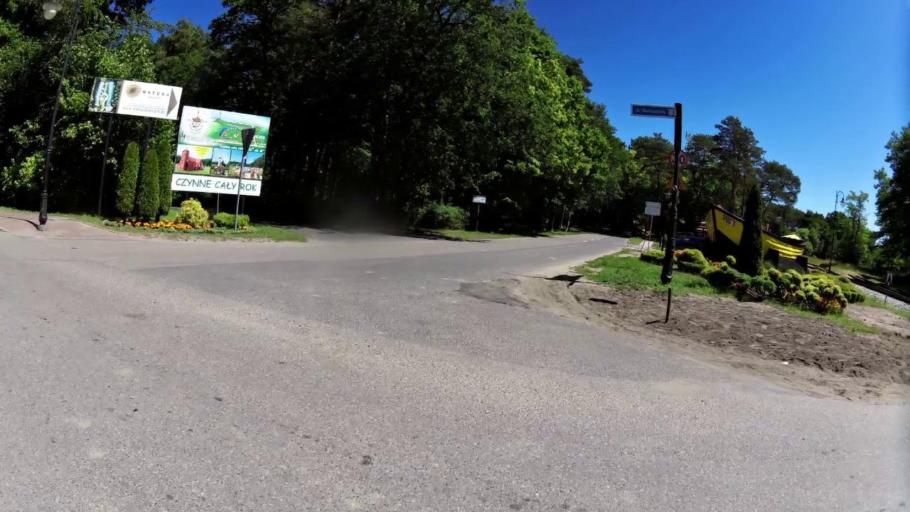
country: PL
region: West Pomeranian Voivodeship
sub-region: Powiat gryficki
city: Cerkwica
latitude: 54.0943
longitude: 15.1235
